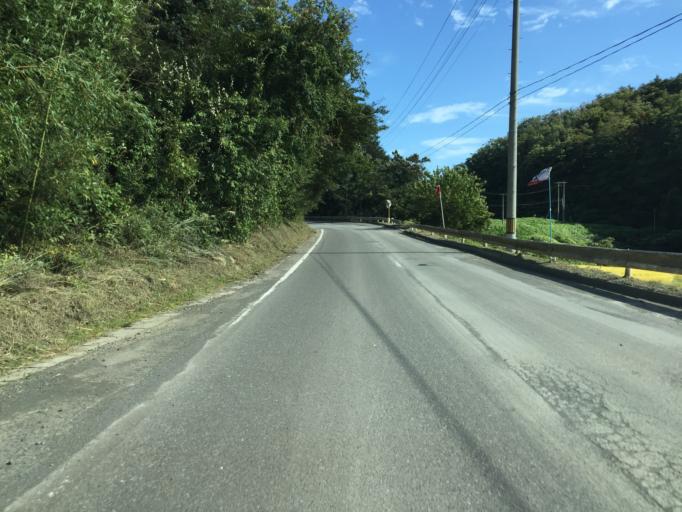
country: JP
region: Fukushima
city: Yanagawamachi-saiwaicho
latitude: 37.8561
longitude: 140.6418
